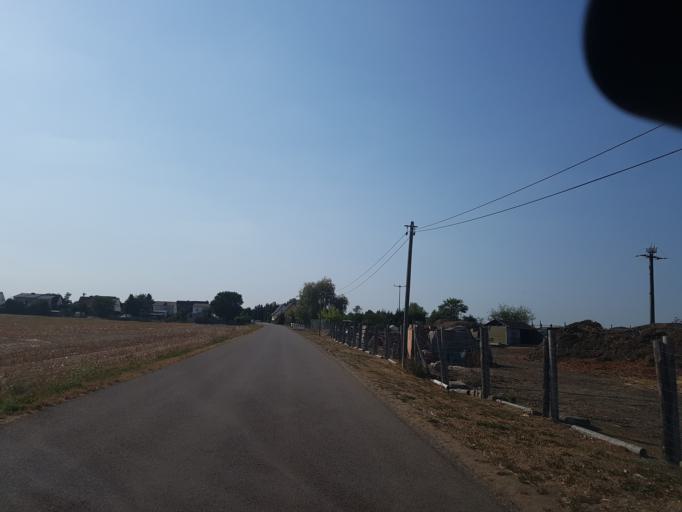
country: DE
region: Saxony
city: Beilrode
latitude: 51.5659
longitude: 13.0820
